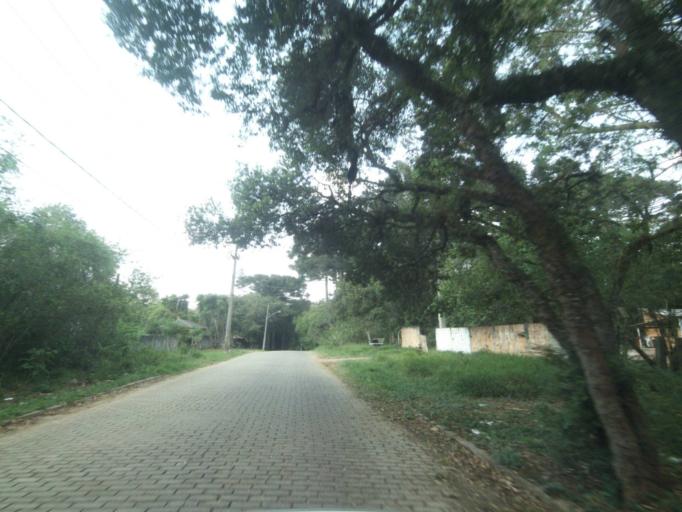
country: BR
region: Parana
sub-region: Sao Jose Dos Pinhais
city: Sao Jose dos Pinhais
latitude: -25.5452
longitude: -49.2401
